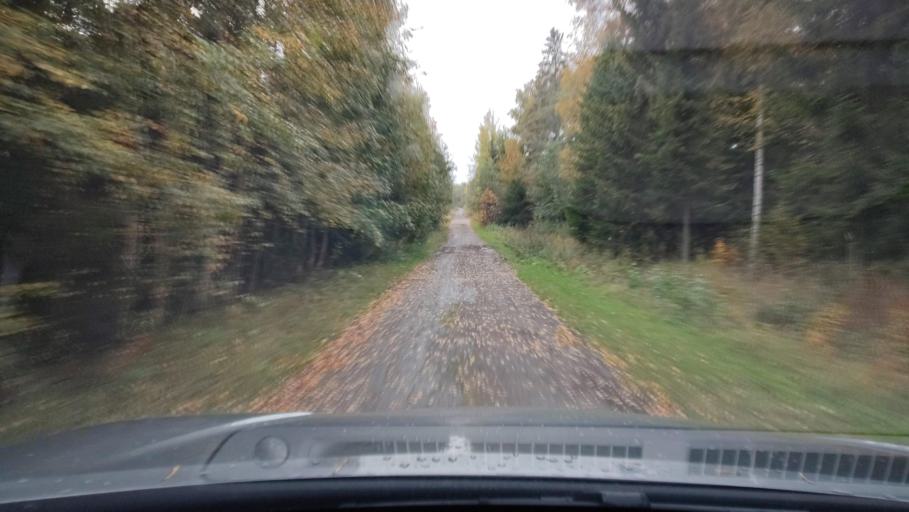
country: FI
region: Ostrobothnia
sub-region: Sydosterbotten
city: Kristinestad
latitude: 62.2662
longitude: 21.4609
